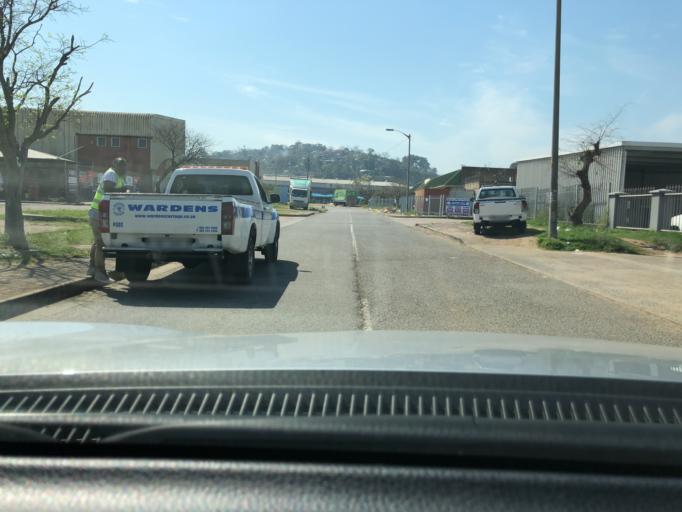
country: ZA
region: KwaZulu-Natal
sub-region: eThekwini Metropolitan Municipality
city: Berea
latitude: -29.8056
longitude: 30.9971
